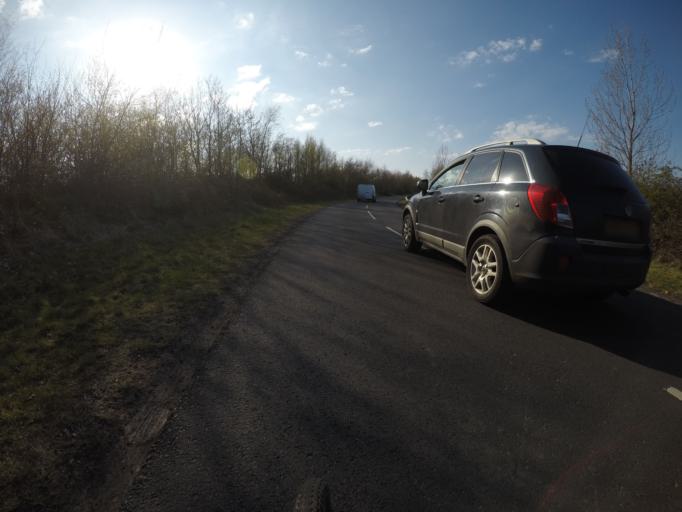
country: GB
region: Scotland
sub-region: North Ayrshire
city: Stevenston
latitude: 55.6500
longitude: -4.7376
